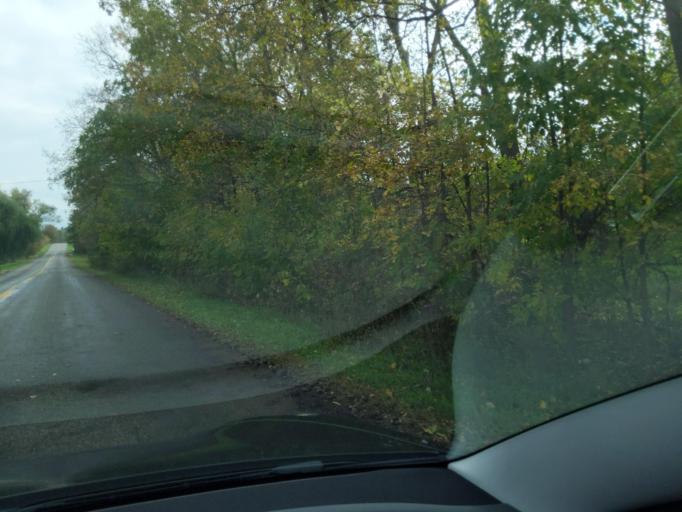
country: US
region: Michigan
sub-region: Eaton County
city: Eaton Rapids
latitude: 42.4724
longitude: -84.6227
